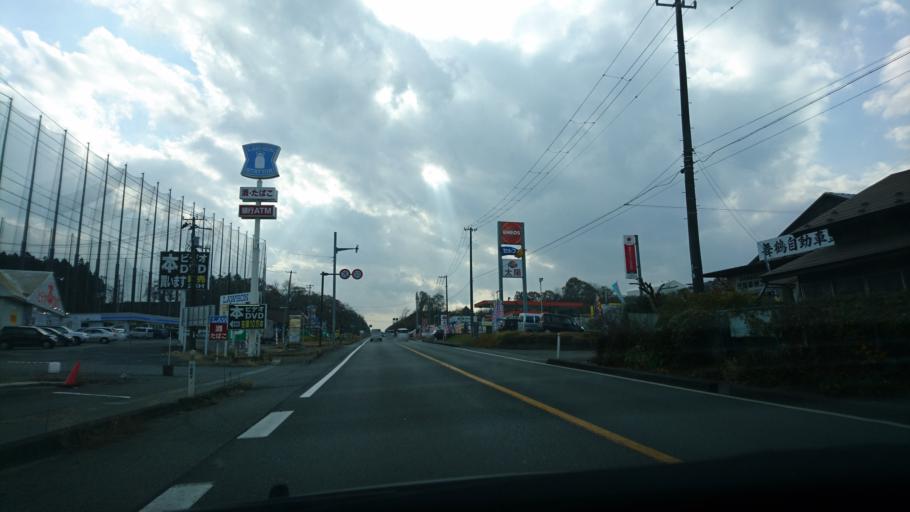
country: JP
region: Iwate
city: Mizusawa
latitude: 39.0329
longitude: 141.1178
